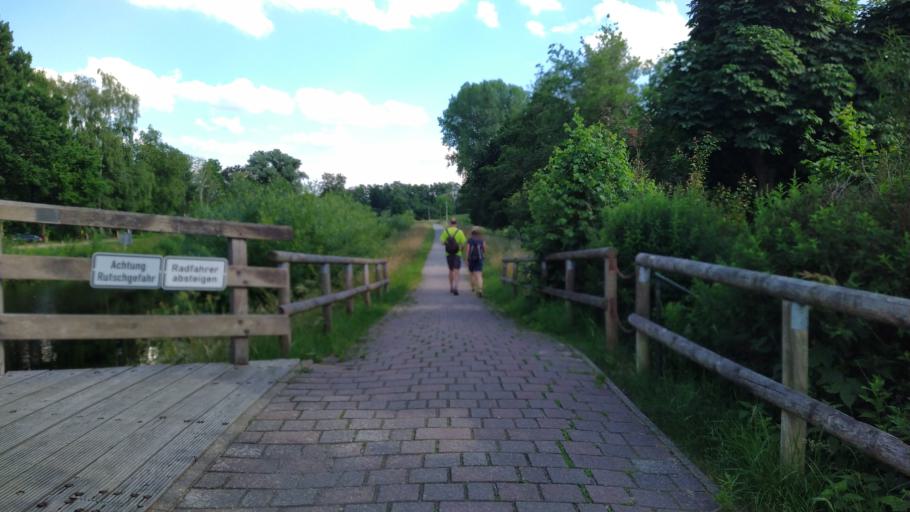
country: DE
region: Lower Saxony
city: Lintig
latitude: 53.6250
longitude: 8.8464
